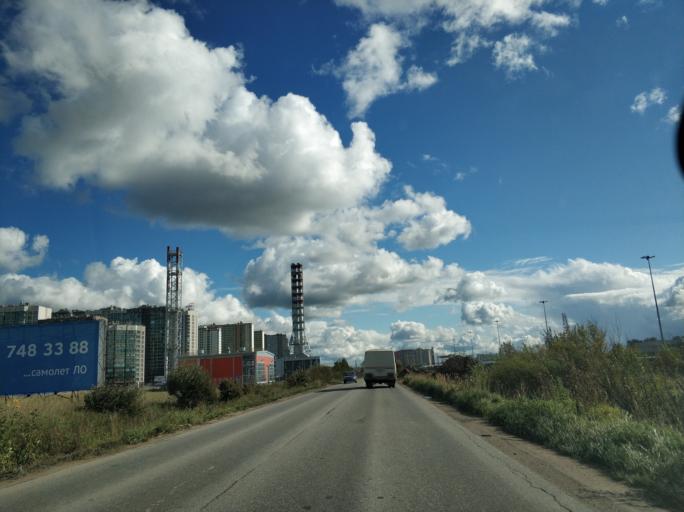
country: RU
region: St.-Petersburg
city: Grazhdanka
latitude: 60.0509
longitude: 30.4133
